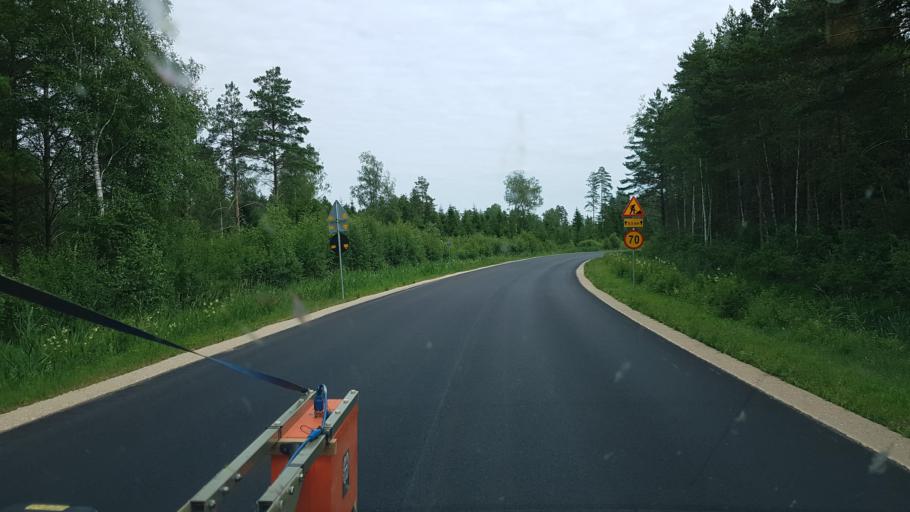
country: EE
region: Paernumaa
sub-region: Audru vald
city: Audru
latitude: 58.6198
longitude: 24.2317
